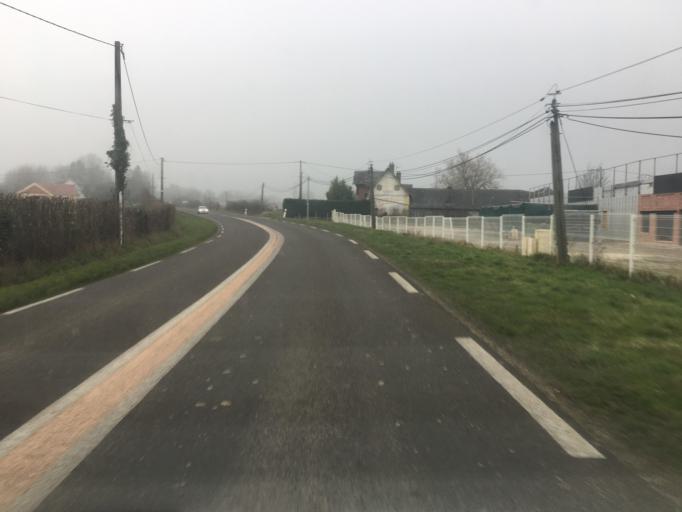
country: FR
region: Haute-Normandie
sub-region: Departement de la Seine-Maritime
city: Neufchatel-en-Bray
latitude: 49.7284
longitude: 1.4263
